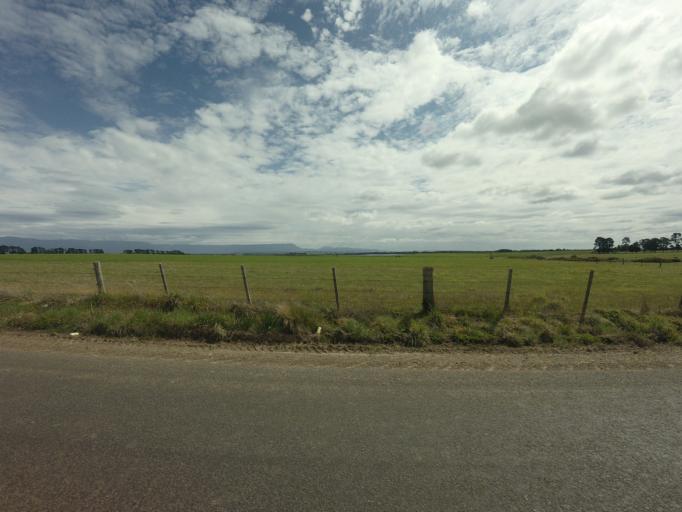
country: AU
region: Tasmania
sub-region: Northern Midlands
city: Longford
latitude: -41.7085
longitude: 147.1961
